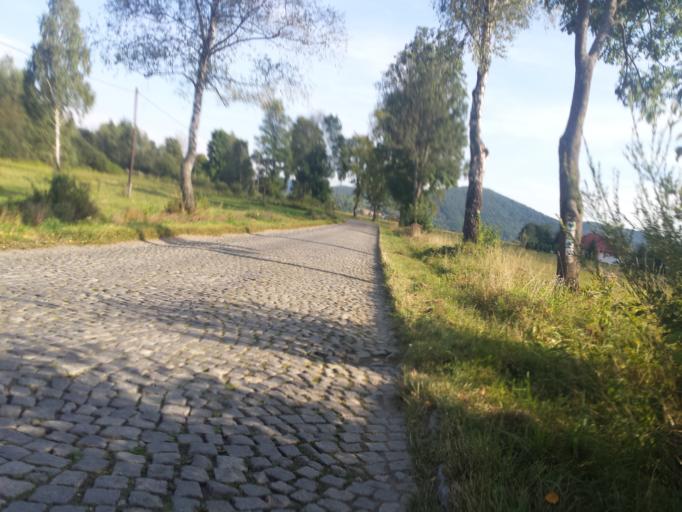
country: PL
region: Subcarpathian Voivodeship
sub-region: Powiat leski
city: Uherce Mineralne
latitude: 49.4470
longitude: 22.3927
